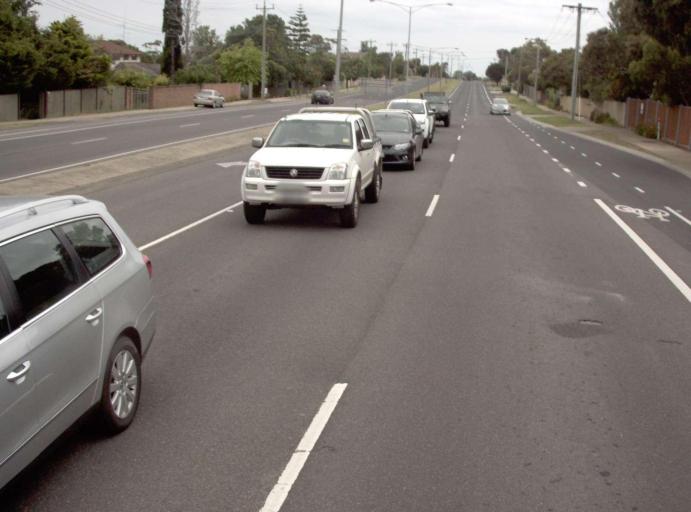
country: AU
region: Victoria
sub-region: Mornington Peninsula
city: Mornington
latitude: -38.2443
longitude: 145.0375
